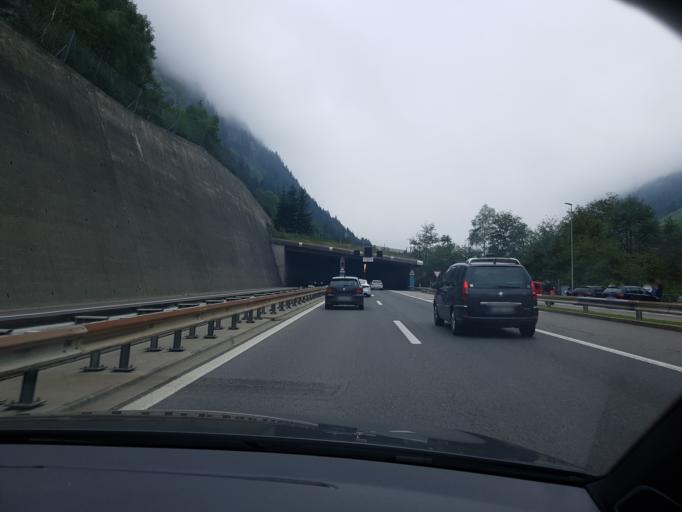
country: CH
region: Uri
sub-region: Uri
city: Silenen
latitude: 46.7264
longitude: 8.6226
